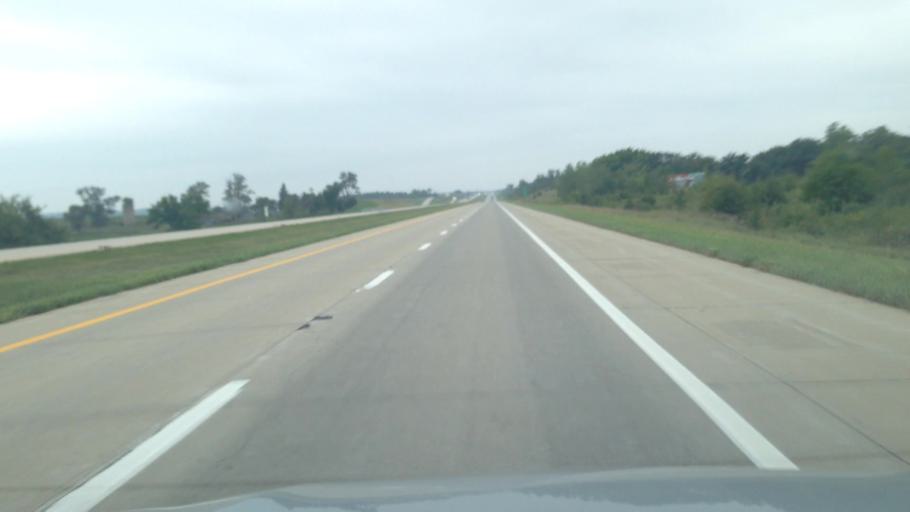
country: US
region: Missouri
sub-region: Harrison County
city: Bethany
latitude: 40.3272
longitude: -94.0117
